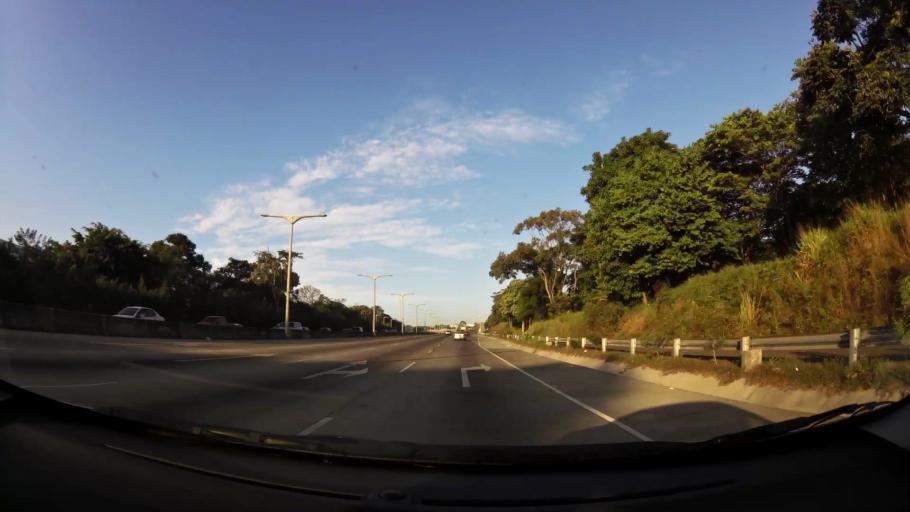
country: SV
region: La Libertad
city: Antiguo Cuscatlan
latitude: 13.6853
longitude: -89.2585
